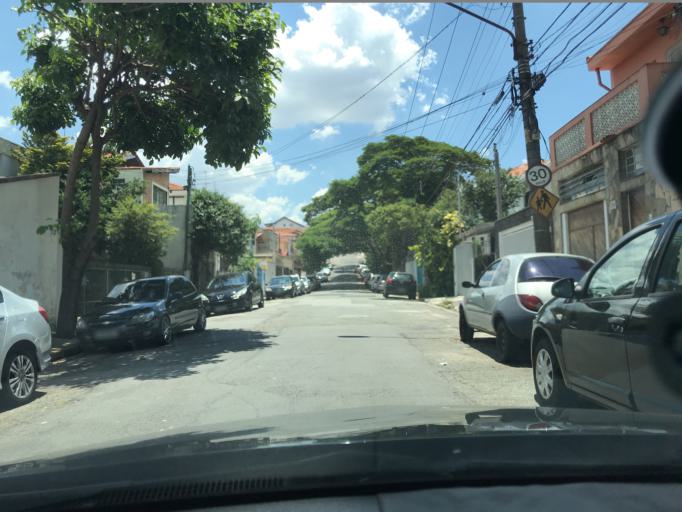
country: BR
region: Sao Paulo
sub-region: Sao Paulo
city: Sao Paulo
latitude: -23.5491
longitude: -46.6976
